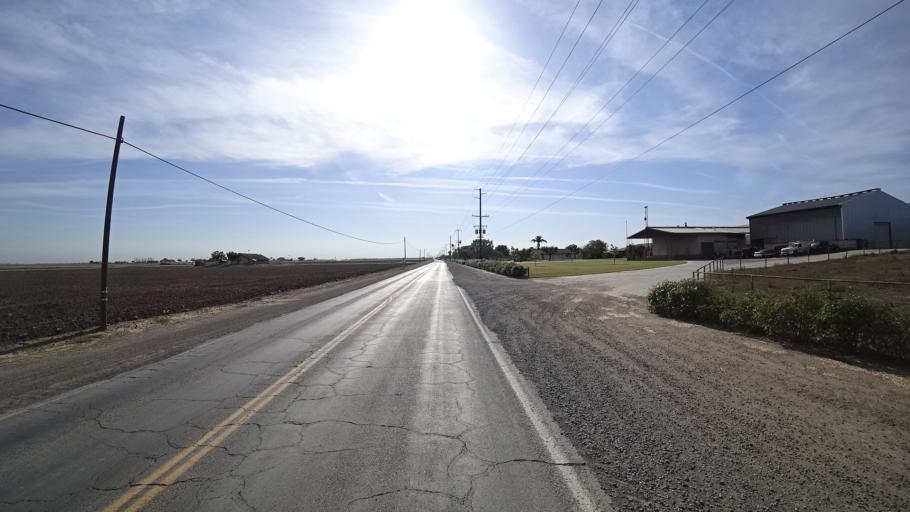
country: US
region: California
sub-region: Tulare County
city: Goshen
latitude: 36.3428
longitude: -119.5224
